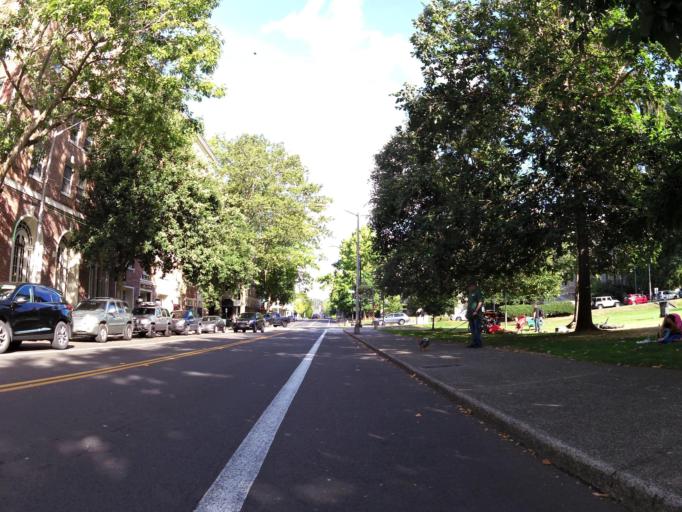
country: US
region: Washington
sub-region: Thurston County
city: Olympia
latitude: 47.0433
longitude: -122.9008
